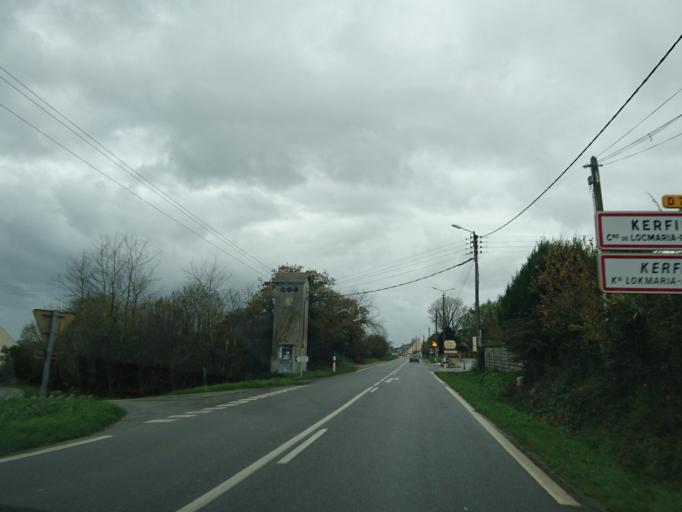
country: FR
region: Brittany
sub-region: Departement du Finistere
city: Plouzane
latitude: 48.3642
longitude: -4.6643
